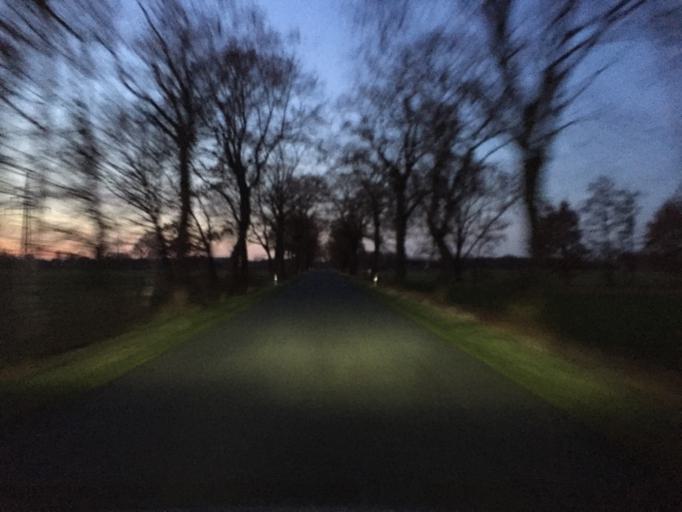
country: DE
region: Lower Saxony
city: Barenburg
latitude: 52.6463
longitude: 8.8248
